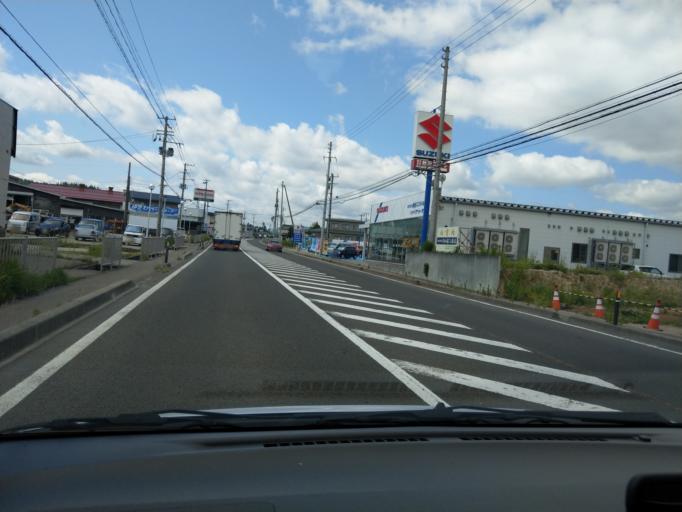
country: JP
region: Akita
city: Yuzawa
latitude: 39.1899
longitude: 140.5016
